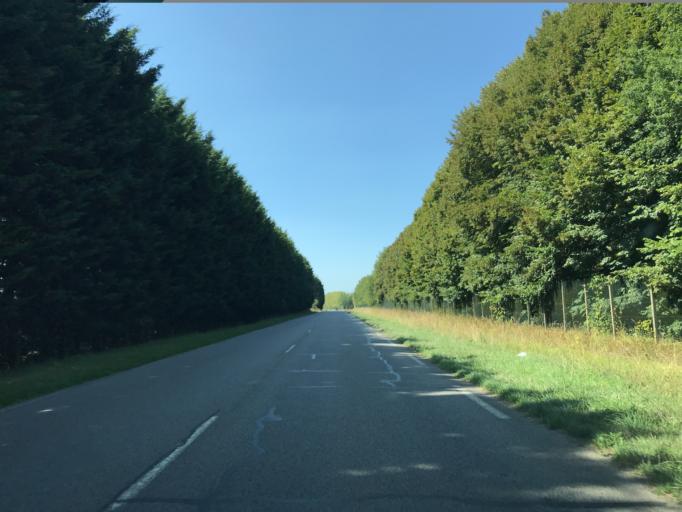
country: FR
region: Haute-Normandie
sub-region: Departement de l'Eure
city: Saint-Just
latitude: 49.0940
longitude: 1.4172
